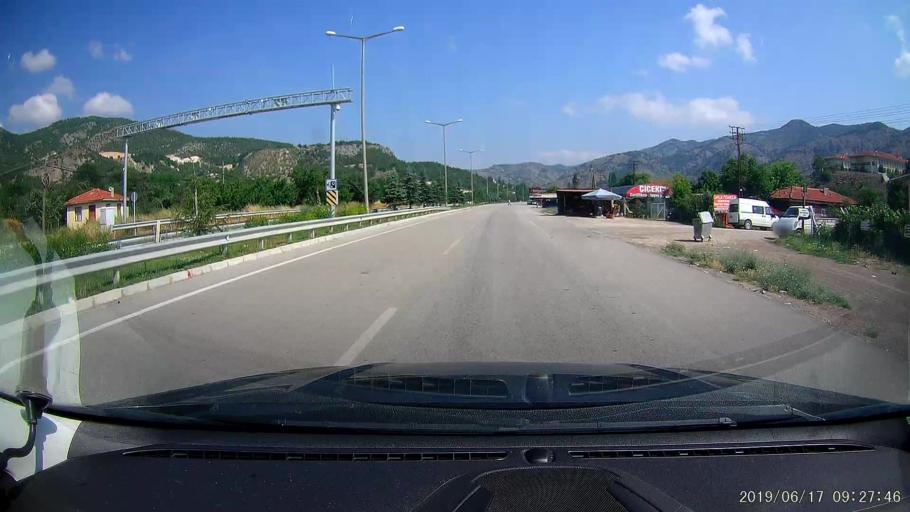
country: TR
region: Amasya
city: Amasya
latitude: 40.6807
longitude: 35.8244
